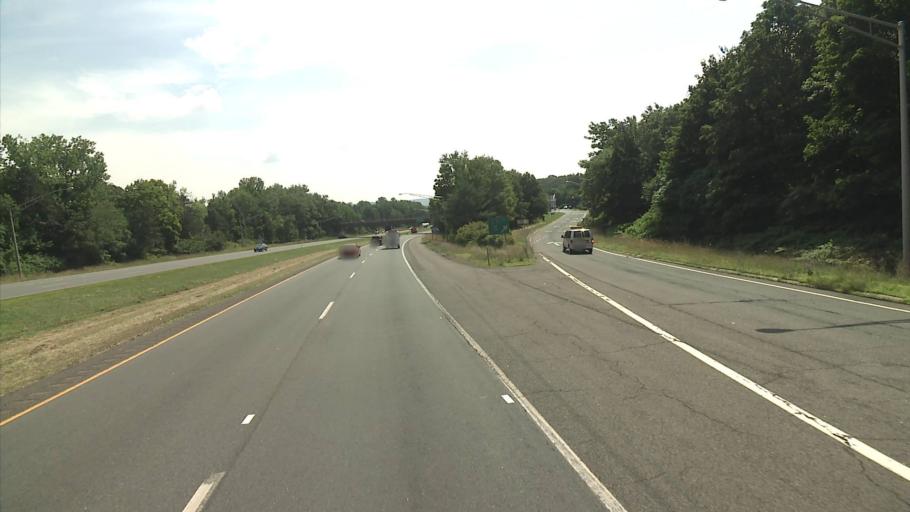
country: US
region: Connecticut
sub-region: New Haven County
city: Meriden
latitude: 41.5497
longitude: -72.8168
